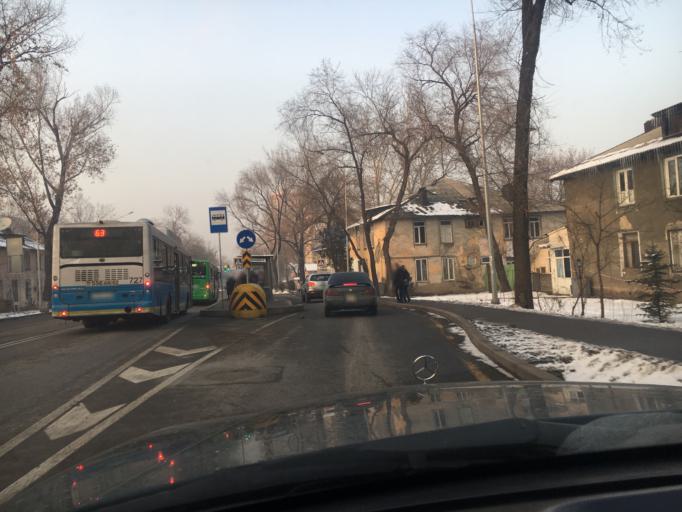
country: KZ
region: Almaty Qalasy
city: Almaty
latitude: 43.2090
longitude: 76.8788
